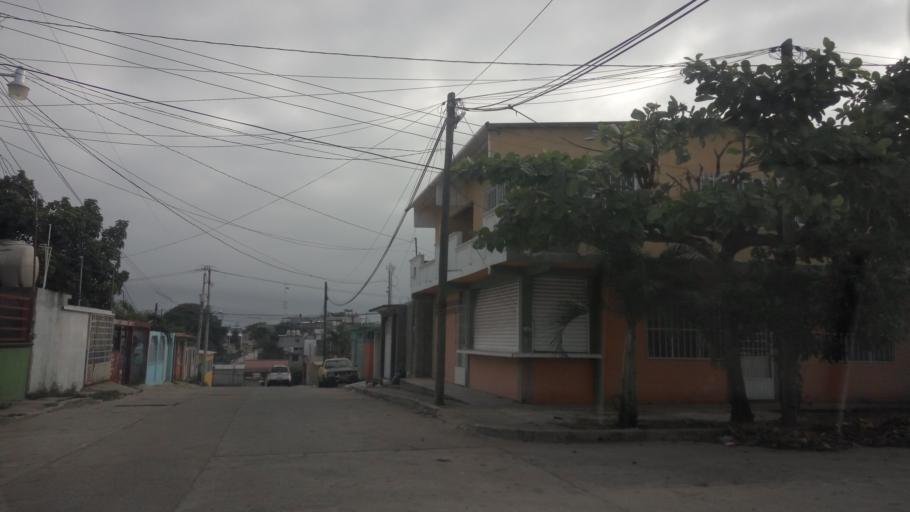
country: MX
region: Chiapas
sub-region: Reforma
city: El Carmen (El Limon)
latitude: 17.8597
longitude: -93.1513
